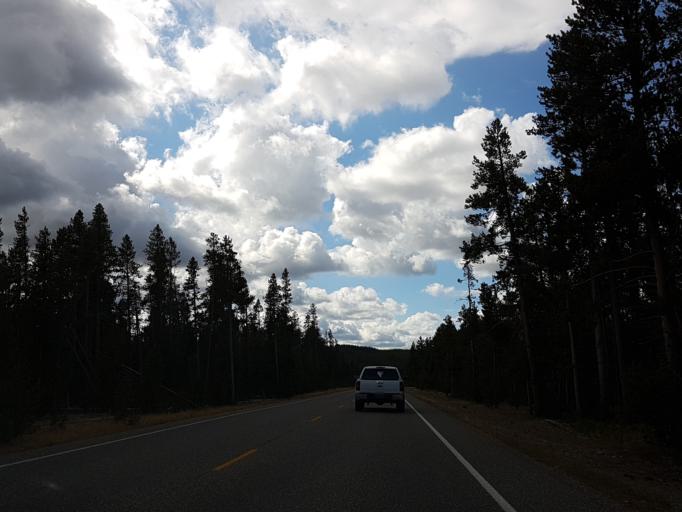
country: US
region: Montana
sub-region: Gallatin County
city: West Yellowstone
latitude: 44.5418
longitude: -110.8122
